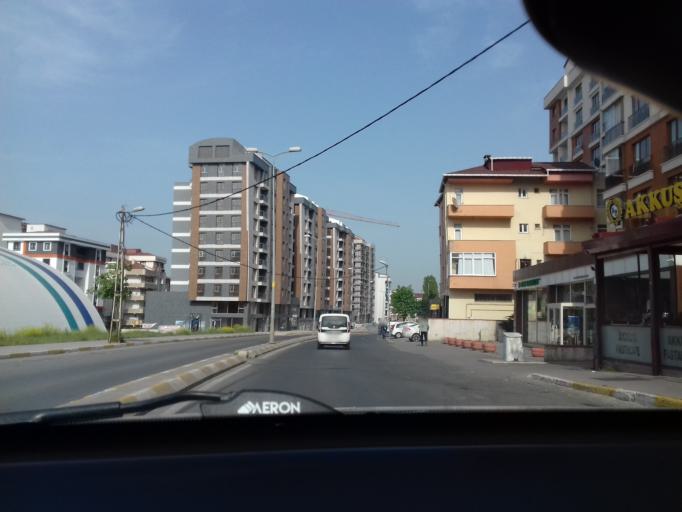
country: TR
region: Istanbul
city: Pendik
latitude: 40.9077
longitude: 29.2559
